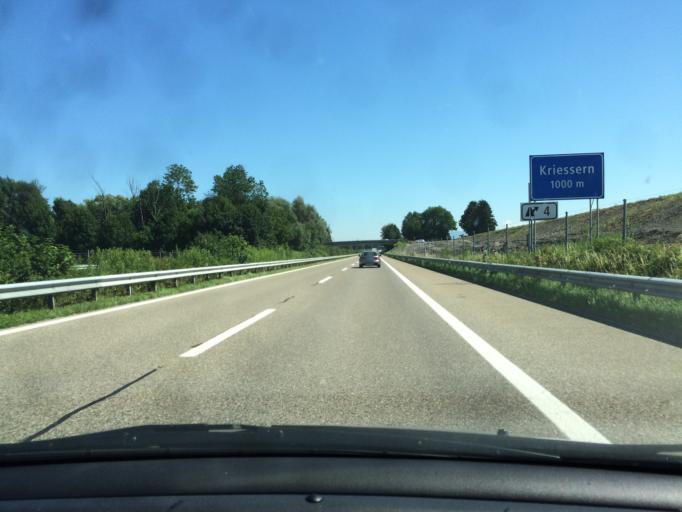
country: AT
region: Vorarlberg
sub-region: Politischer Bezirk Feldkirch
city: Koblach
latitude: 47.3468
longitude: 9.5975
